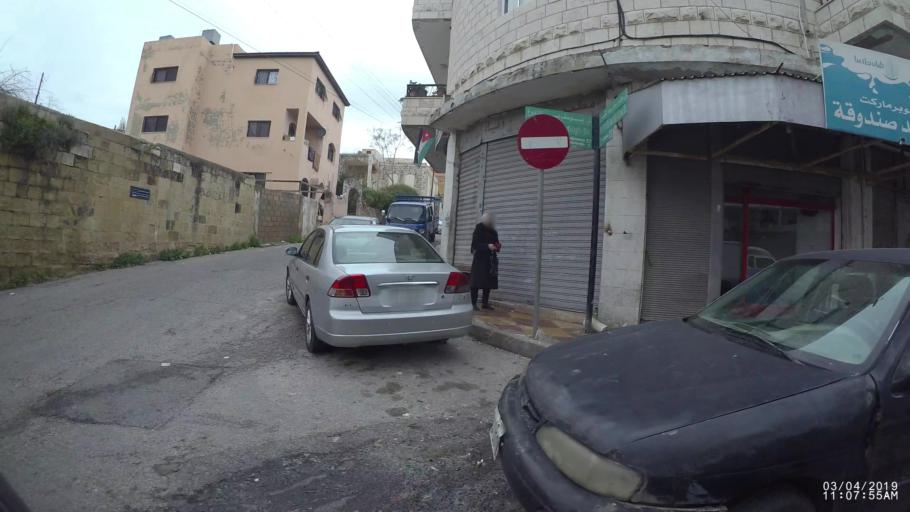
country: JO
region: Amman
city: Wadi as Sir
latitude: 31.9513
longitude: 35.8172
